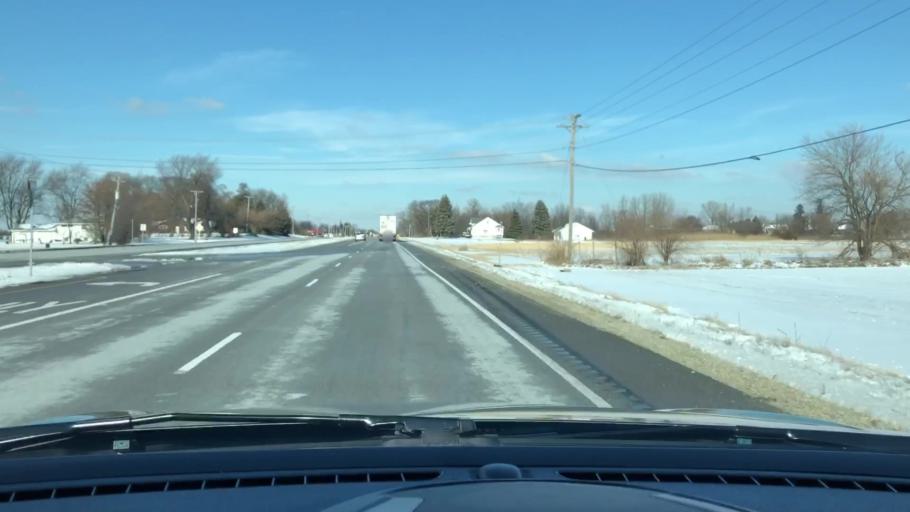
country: US
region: Illinois
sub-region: Will County
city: Preston Heights
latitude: 41.4731
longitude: -88.0798
